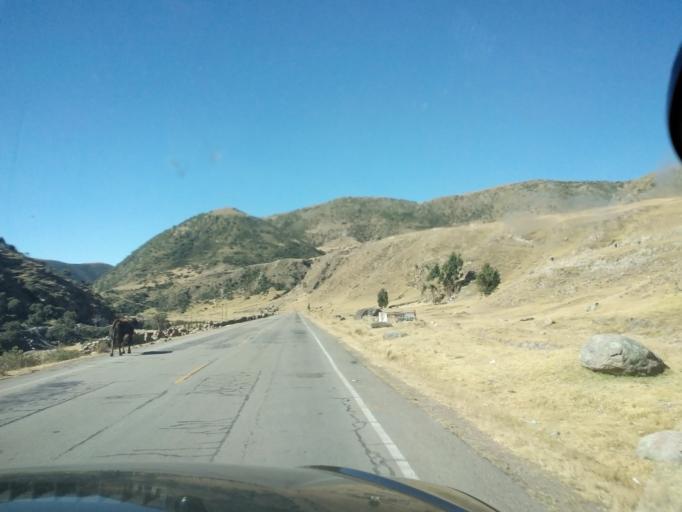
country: PE
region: Ayacucho
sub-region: Provincia de Huamanga
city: Vinchos
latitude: -13.3536
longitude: -74.4016
